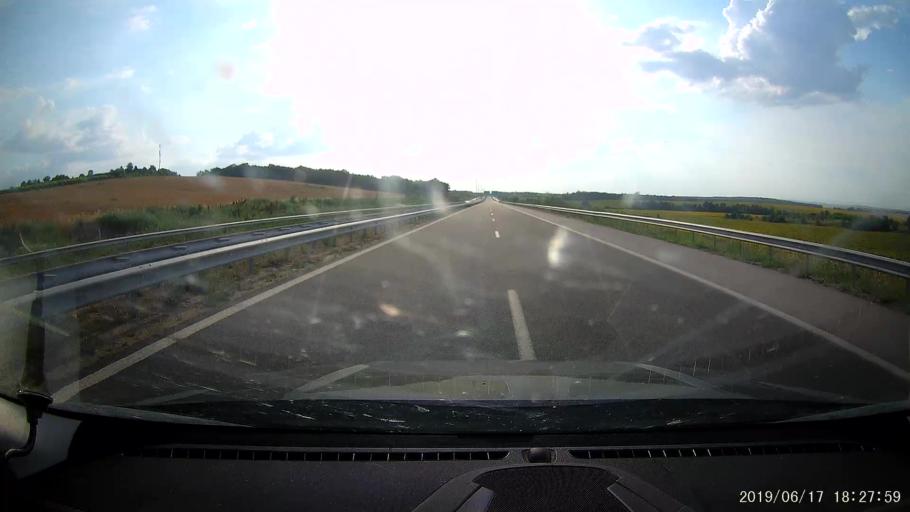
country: BG
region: Khaskovo
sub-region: Obshtina Dimitrovgrad
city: Dimitrovgrad
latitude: 42.0199
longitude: 25.5935
